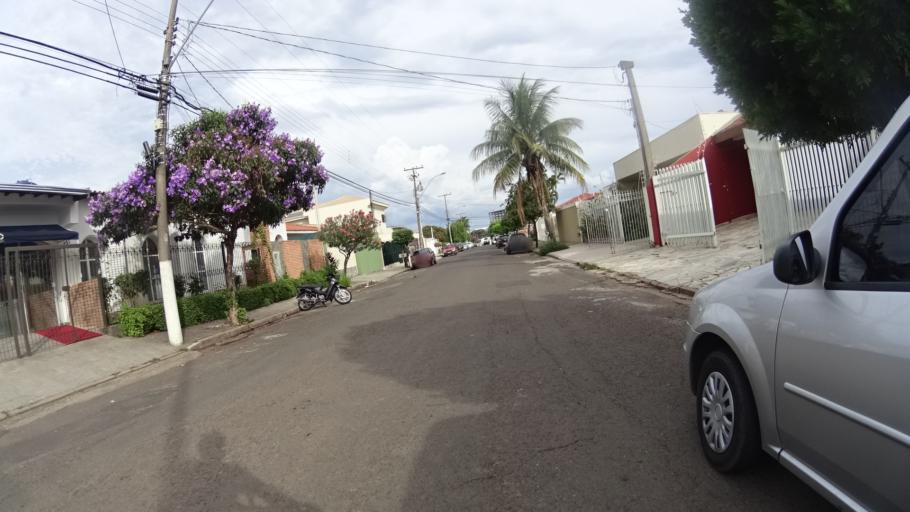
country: BR
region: Sao Paulo
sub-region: Marilia
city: Marilia
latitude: -22.2218
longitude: -49.9370
